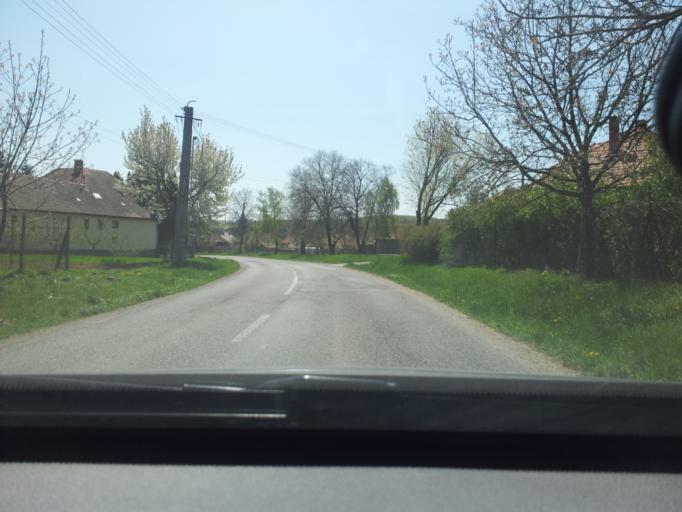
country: SK
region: Nitriansky
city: Zlate Moravce
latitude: 48.3095
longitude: 18.4443
